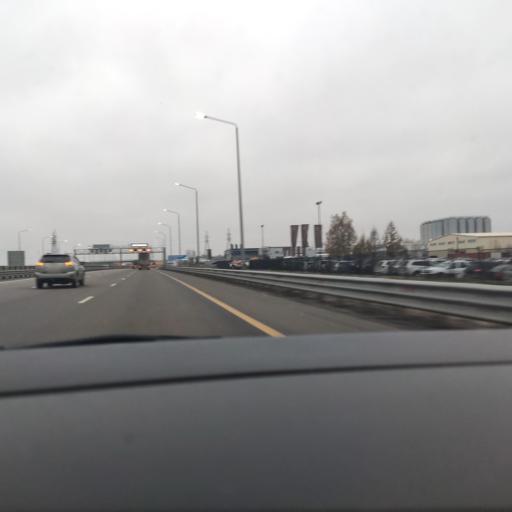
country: RU
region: Voronezj
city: Somovo
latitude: 51.6727
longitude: 39.3006
